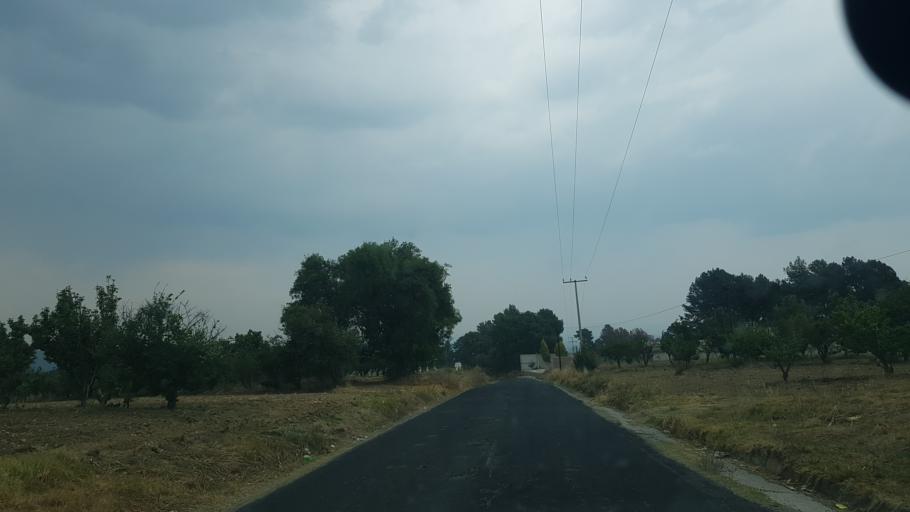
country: MX
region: Puebla
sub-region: Chiautzingo
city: San Nicolas Zecalacoayan
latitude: 19.1870
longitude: -98.4774
